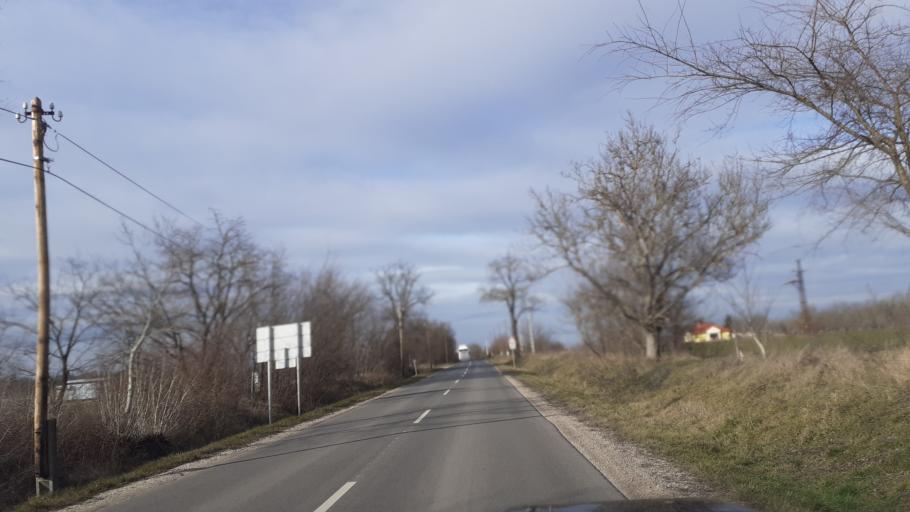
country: HU
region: Fejer
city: Kaloz
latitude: 46.9678
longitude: 18.4830
